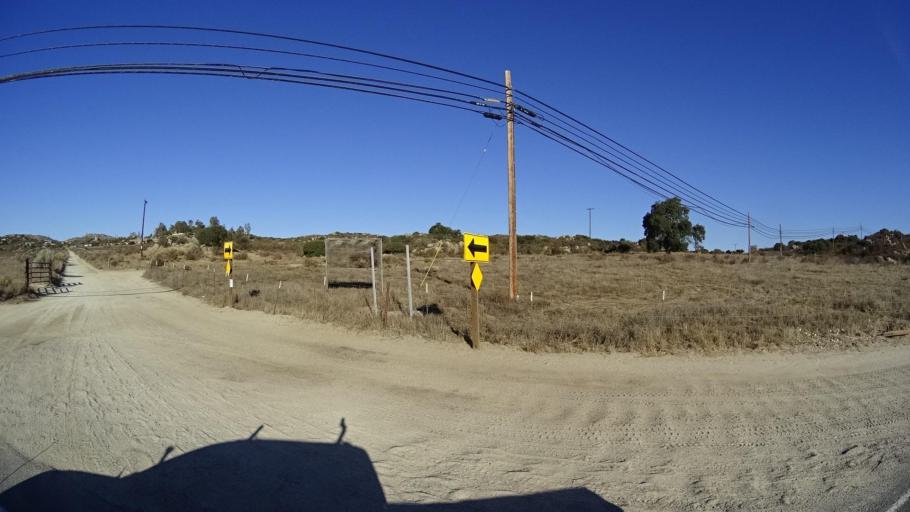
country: US
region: California
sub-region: San Diego County
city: Campo
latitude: 32.6217
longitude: -116.4756
